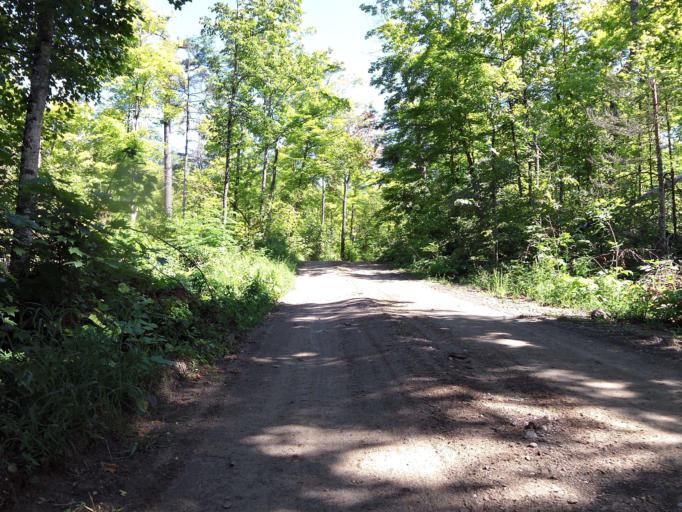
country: CA
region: Ontario
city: Renfrew
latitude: 45.1280
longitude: -76.7205
